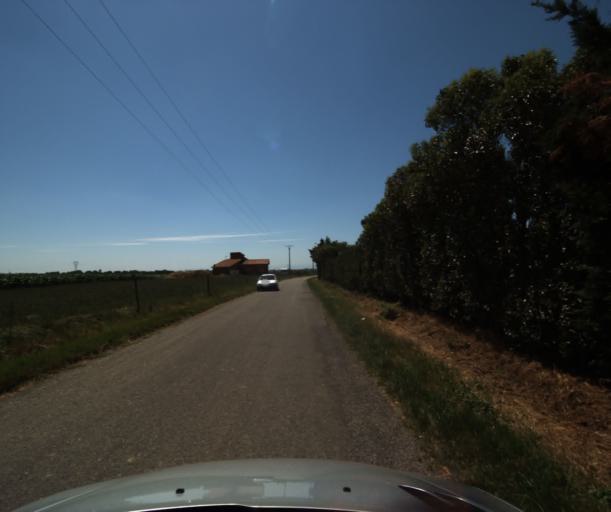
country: FR
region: Midi-Pyrenees
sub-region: Departement de la Haute-Garonne
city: Roquettes
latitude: 43.4884
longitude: 1.3682
